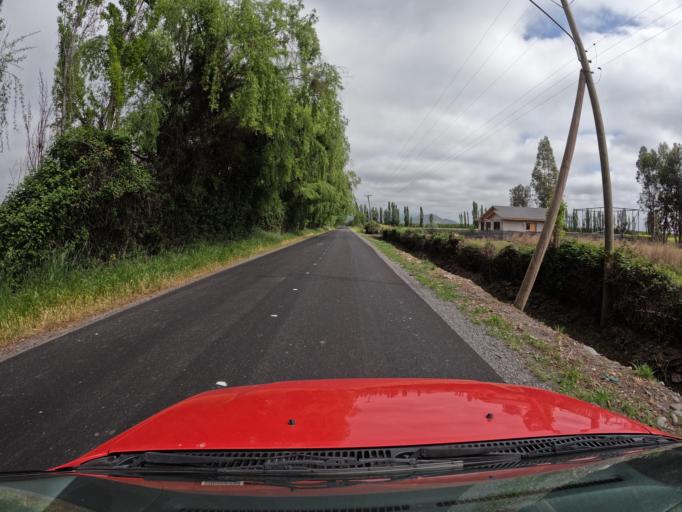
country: CL
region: O'Higgins
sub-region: Provincia de Colchagua
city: Santa Cruz
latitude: -34.6706
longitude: -71.3831
